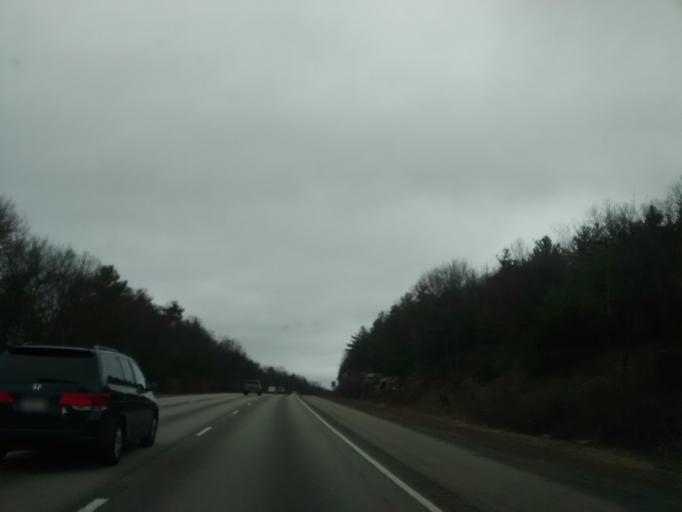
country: US
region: Massachusetts
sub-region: Middlesex County
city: Hopkinton
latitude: 42.1867
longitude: -71.5330
